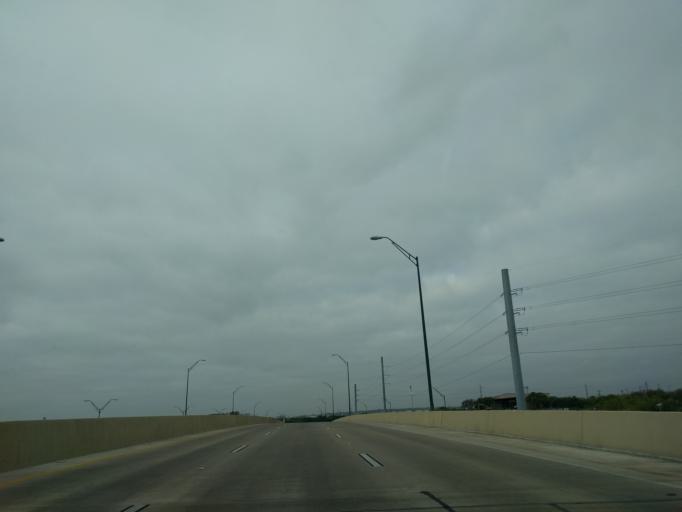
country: US
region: Texas
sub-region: Bexar County
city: Alamo Heights
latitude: 29.5458
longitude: -98.4544
